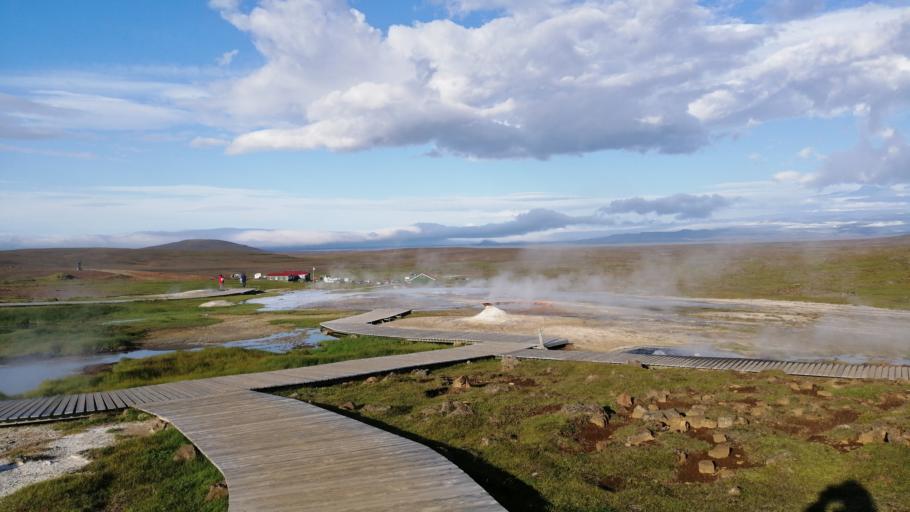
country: IS
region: Northwest
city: Saudarkrokur
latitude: 64.8649
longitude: -19.5594
